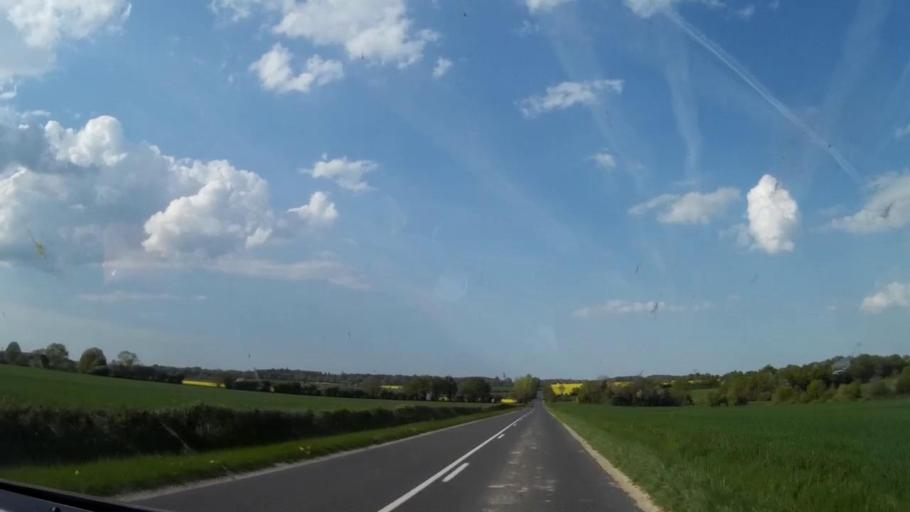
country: FR
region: Centre
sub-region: Departement du Loir-et-Cher
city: Mondoubleau
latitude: 47.9151
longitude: 0.9315
